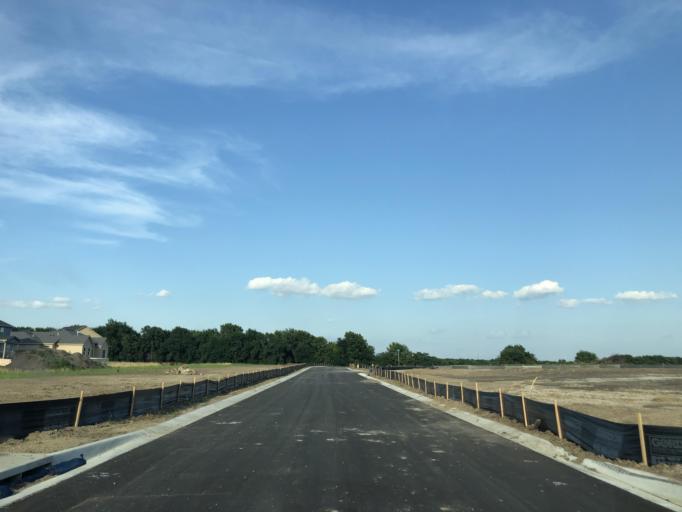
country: US
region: Kansas
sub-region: Johnson County
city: Gardner
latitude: 38.8296
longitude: -94.9582
